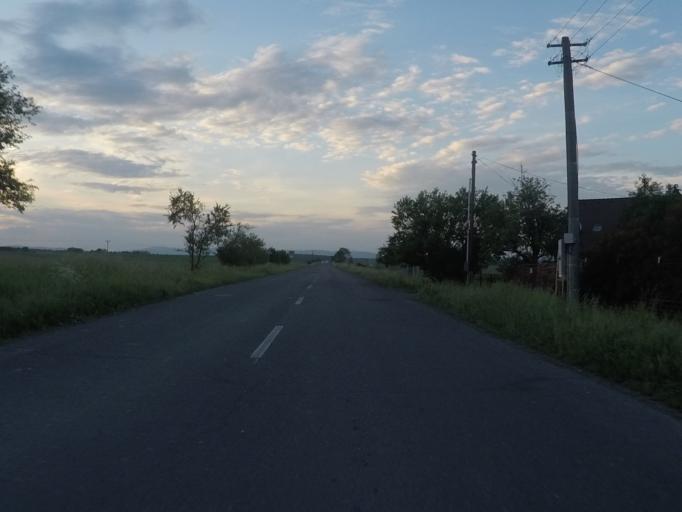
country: SK
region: Banskobystricky
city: Fil'akovo
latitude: 48.3528
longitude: 19.8330
